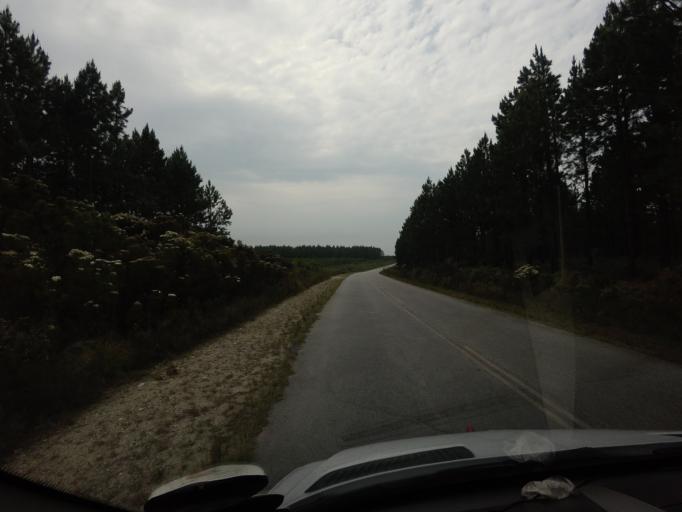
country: ZA
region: Eastern Cape
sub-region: Cacadu District Municipality
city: Kareedouw
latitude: -33.9955
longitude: 23.8513
